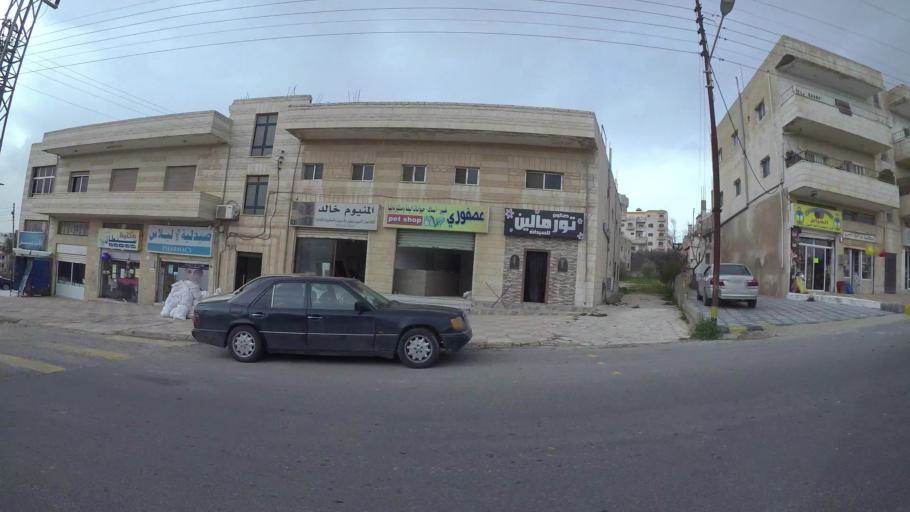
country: JO
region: Amman
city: Umm as Summaq
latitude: 31.9054
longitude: 35.8370
